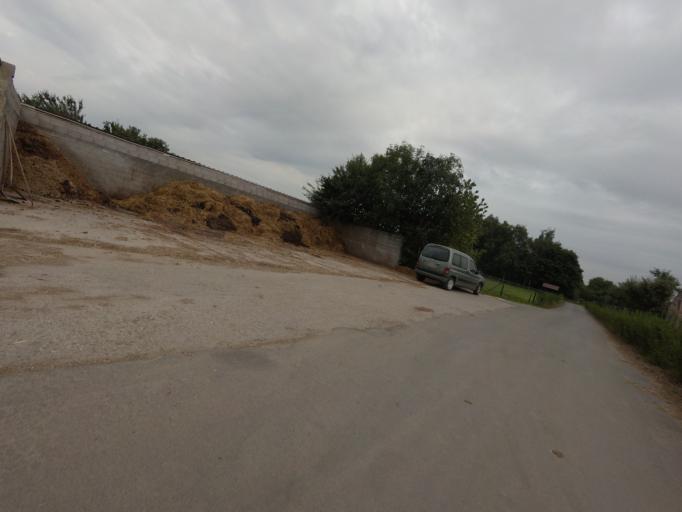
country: BE
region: Flanders
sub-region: Provincie Vlaams-Brabant
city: Kampenhout
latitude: 50.9431
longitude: 4.5541
